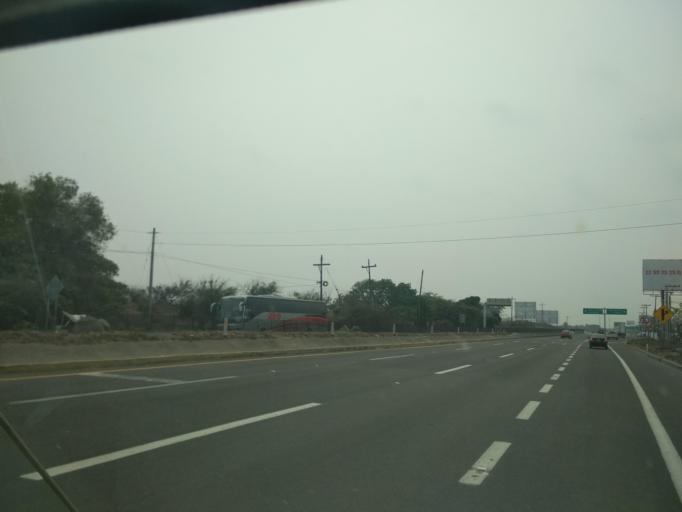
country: MX
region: Veracruz
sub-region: Veracruz
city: Fraccionamiento Geovillas los Pinos
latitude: 19.2203
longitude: -96.2253
